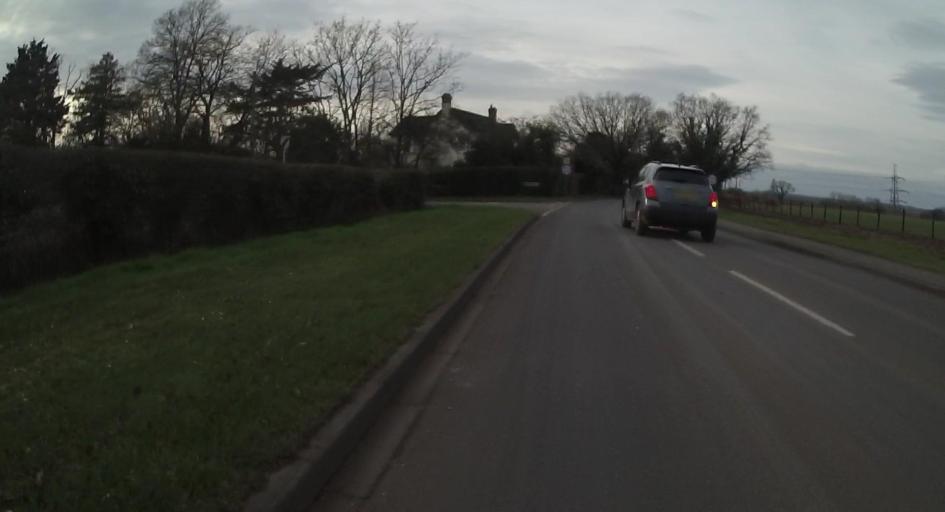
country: GB
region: England
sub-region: West Berkshire
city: Calcot
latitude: 51.4168
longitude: -1.0574
